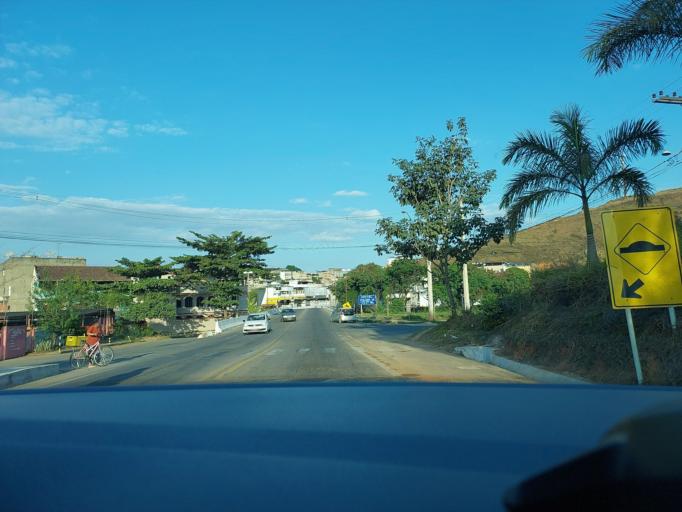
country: BR
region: Minas Gerais
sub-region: Muriae
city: Muriae
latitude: -21.1293
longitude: -42.3965
